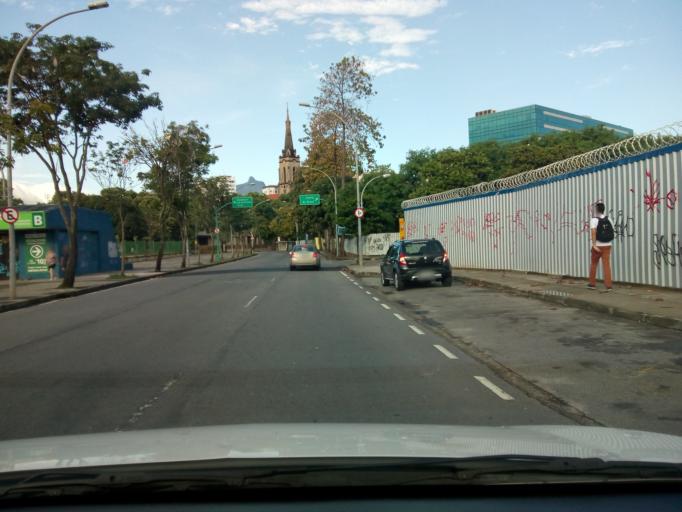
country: BR
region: Rio de Janeiro
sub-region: Rio De Janeiro
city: Rio de Janeiro
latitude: -22.9130
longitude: -43.2071
